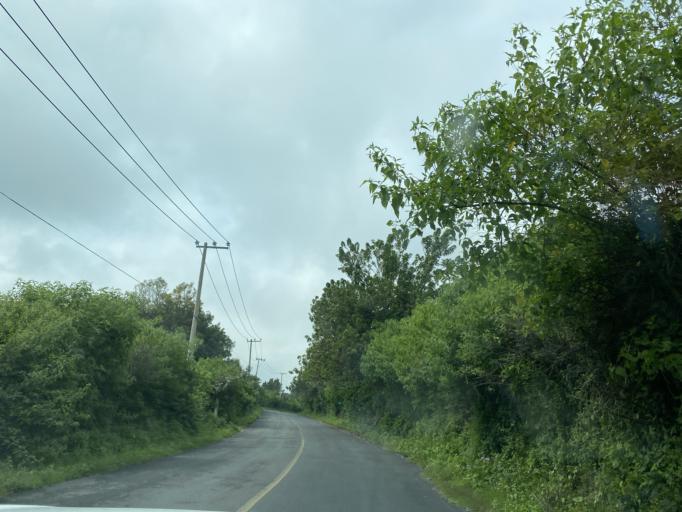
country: MX
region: Mexico
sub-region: Ozumba
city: San Jose Tlacotitlan
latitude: 18.9963
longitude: -98.8027
